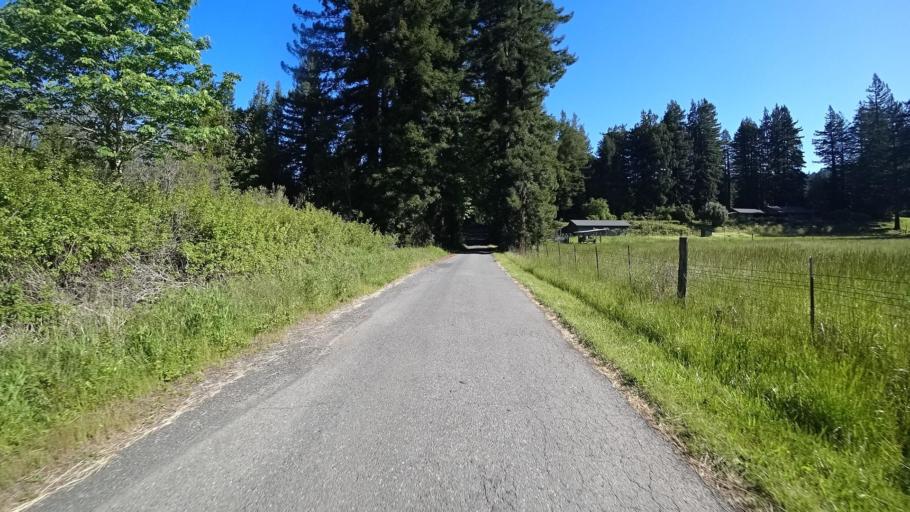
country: US
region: California
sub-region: Humboldt County
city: Rio Dell
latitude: 40.4322
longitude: -123.9691
